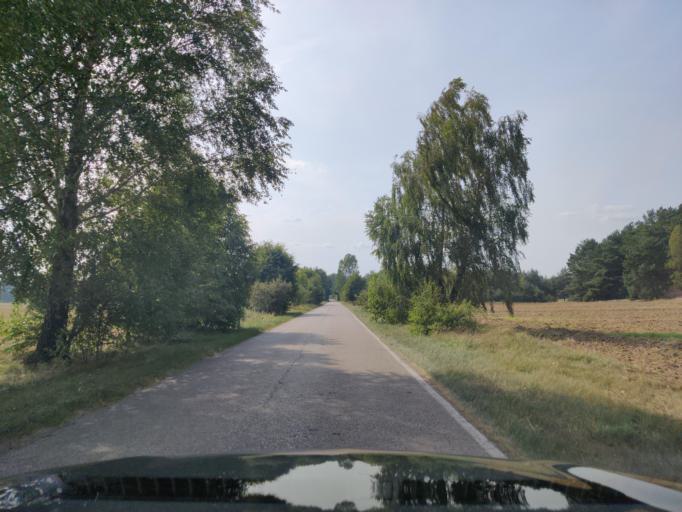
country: PL
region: Masovian Voivodeship
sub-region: Powiat wyszkowski
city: Rzasnik
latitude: 52.7652
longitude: 21.3761
